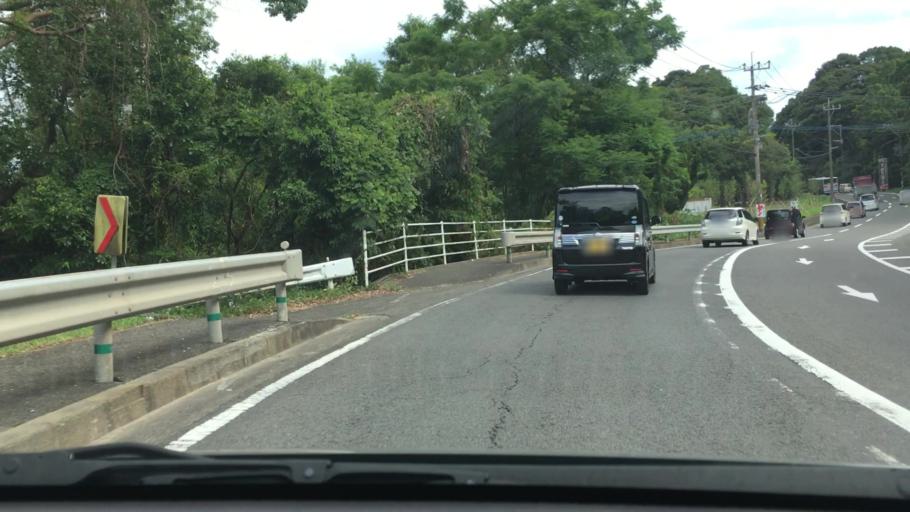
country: JP
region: Nagasaki
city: Togitsu
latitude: 32.9269
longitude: 129.7863
